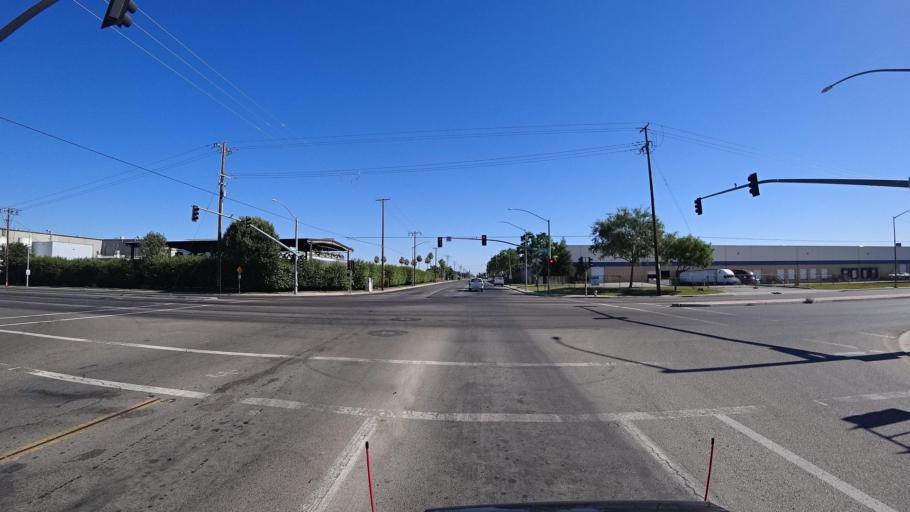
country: US
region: California
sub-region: Fresno County
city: Easton
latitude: 36.6921
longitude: -119.7817
